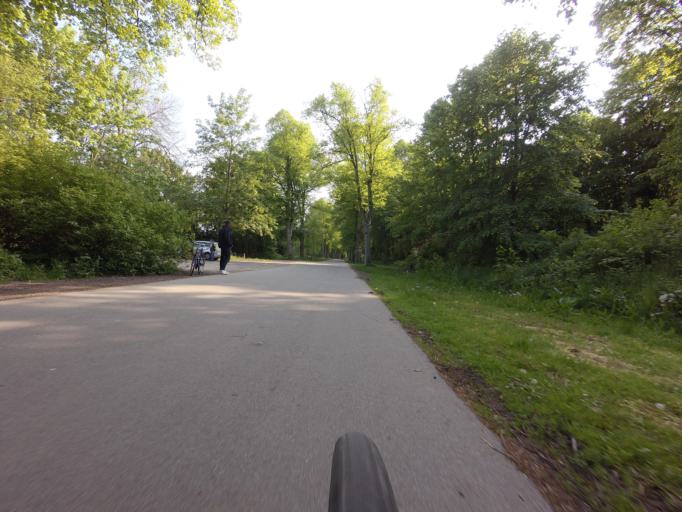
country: DK
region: Capital Region
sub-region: Rodovre Kommune
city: Rodovre
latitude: 55.6873
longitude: 12.4352
